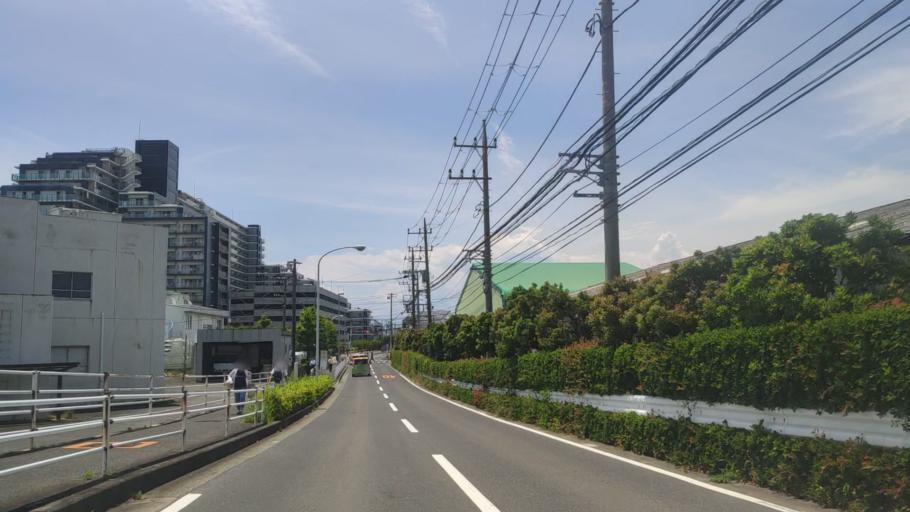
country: JP
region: Kanagawa
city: Chigasaki
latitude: 35.3347
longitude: 139.4008
